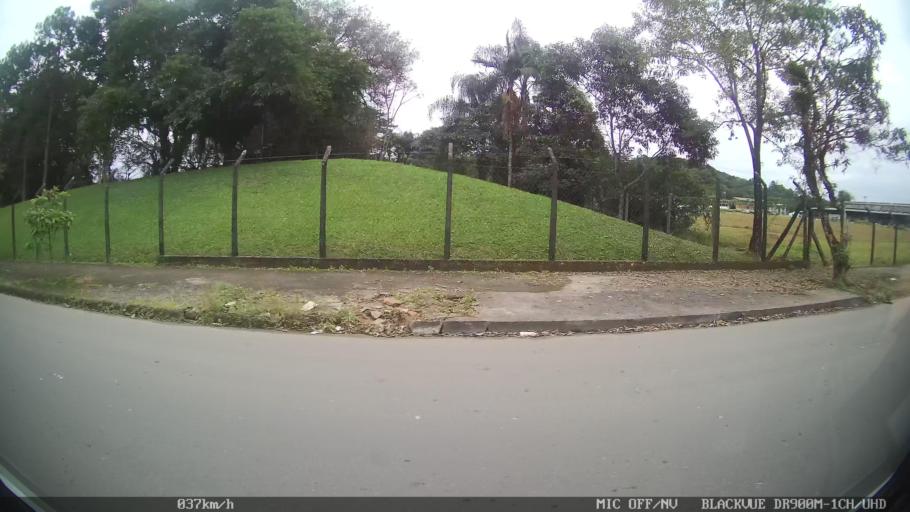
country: BR
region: Santa Catarina
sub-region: Joinville
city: Joinville
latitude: -26.2645
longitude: -48.8882
